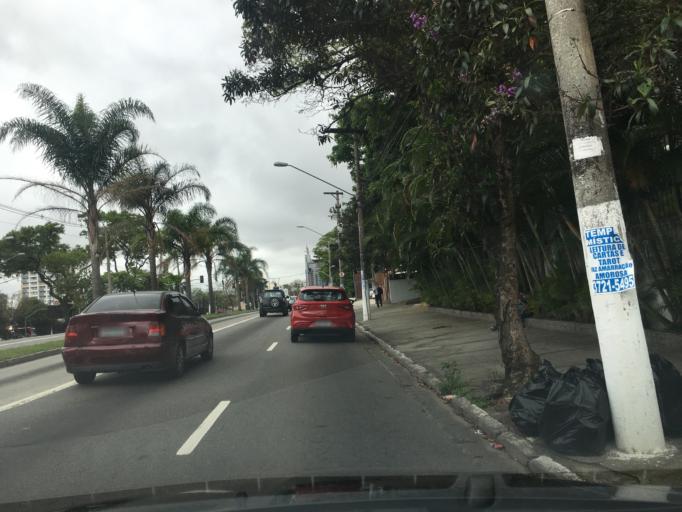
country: BR
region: Sao Paulo
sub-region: Sao Paulo
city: Sao Paulo
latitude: -23.5761
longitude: -46.7074
